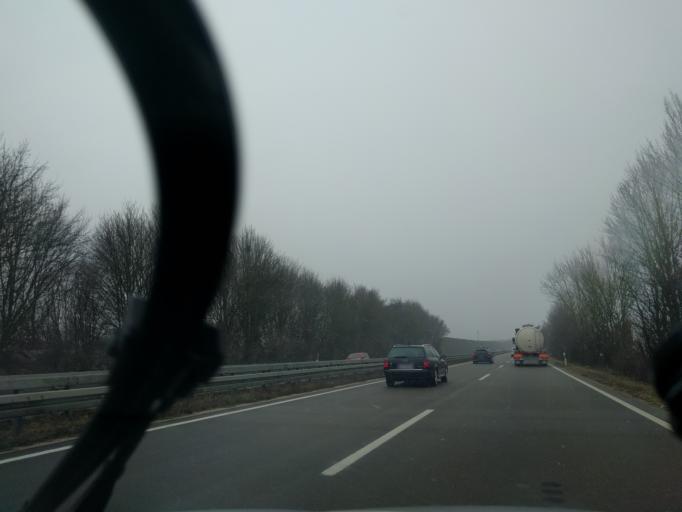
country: DE
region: Bavaria
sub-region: Swabia
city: Asbach-Baumenheim
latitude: 48.6866
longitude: 10.8190
